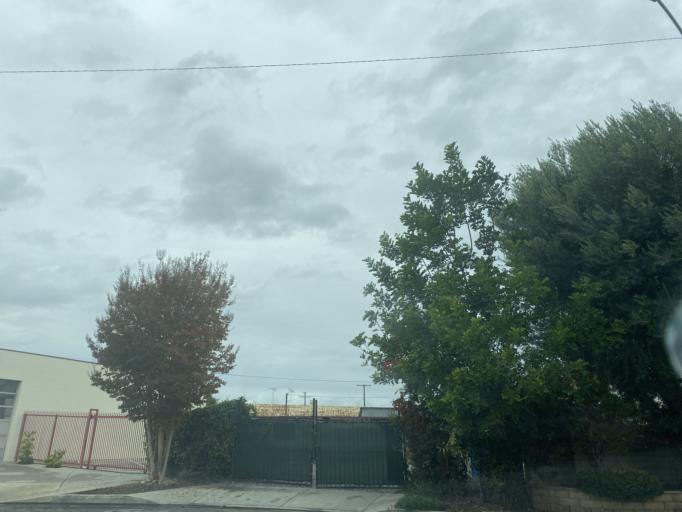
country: US
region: California
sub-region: Orange County
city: Fullerton
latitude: 33.8690
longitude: -117.9141
